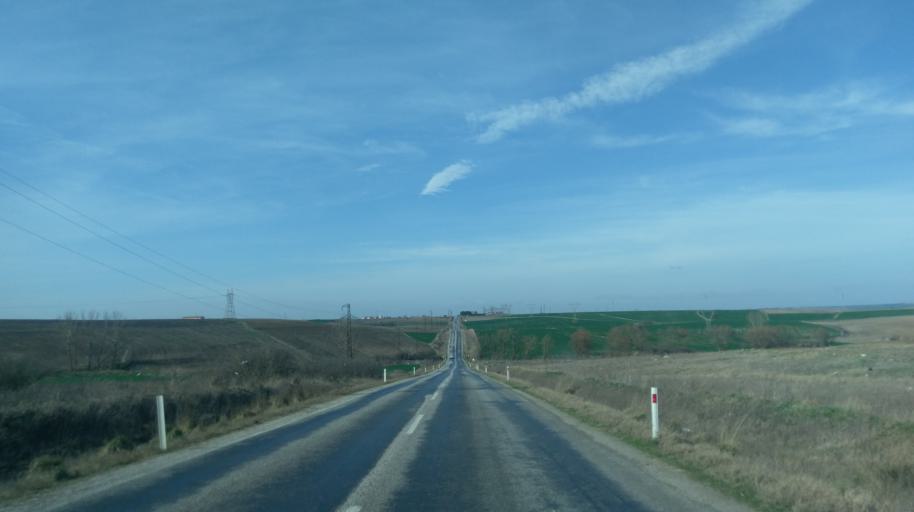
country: TR
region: Edirne
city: Uzun Keupru
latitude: 41.2729
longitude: 26.7308
